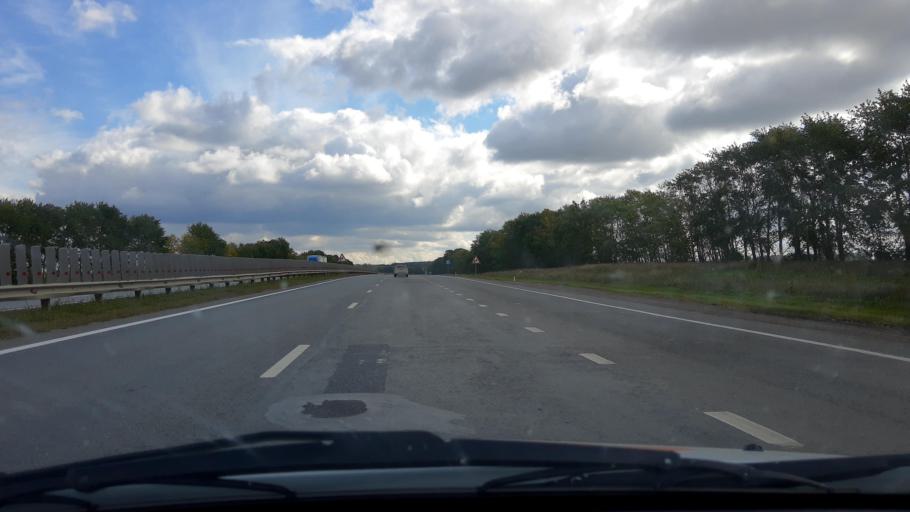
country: RU
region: Bashkortostan
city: Alekseyevka
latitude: 54.7308
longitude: 55.0364
